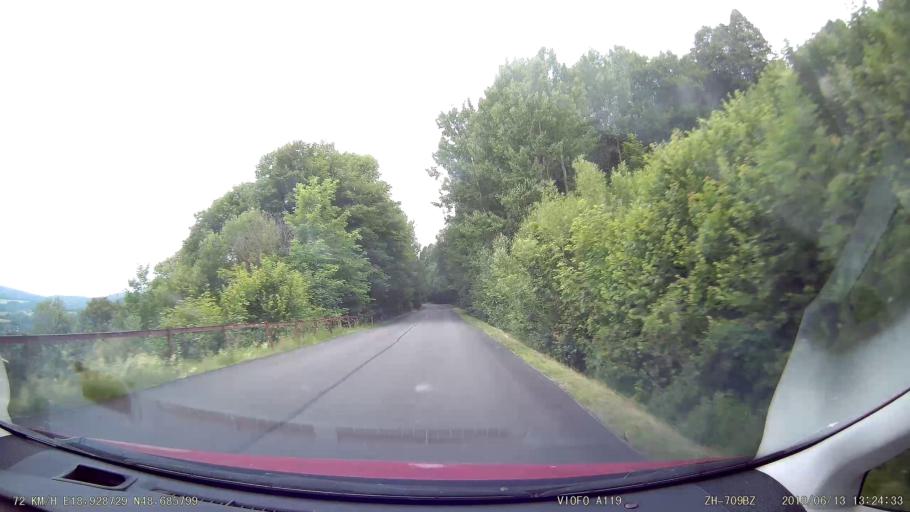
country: SK
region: Banskobystricky
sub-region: Okres Ziar nad Hronom
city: Kremnica
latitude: 48.6860
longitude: 18.9287
